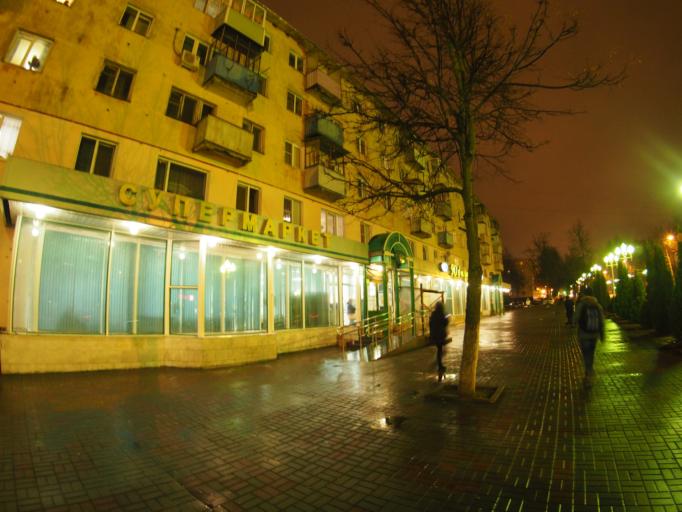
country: RU
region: Moskovskaya
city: Stupino
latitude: 54.8948
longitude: 38.0795
